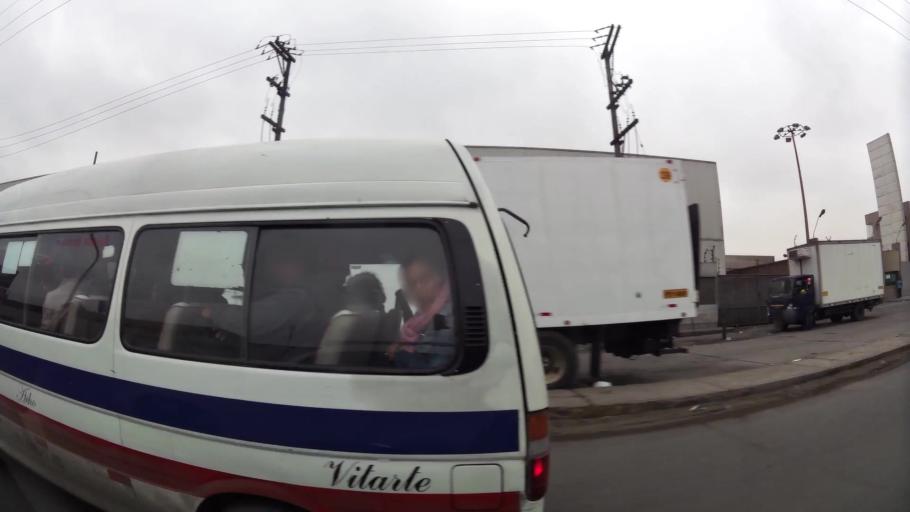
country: PE
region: Lima
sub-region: Lima
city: Vitarte
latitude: -12.0500
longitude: -76.9536
